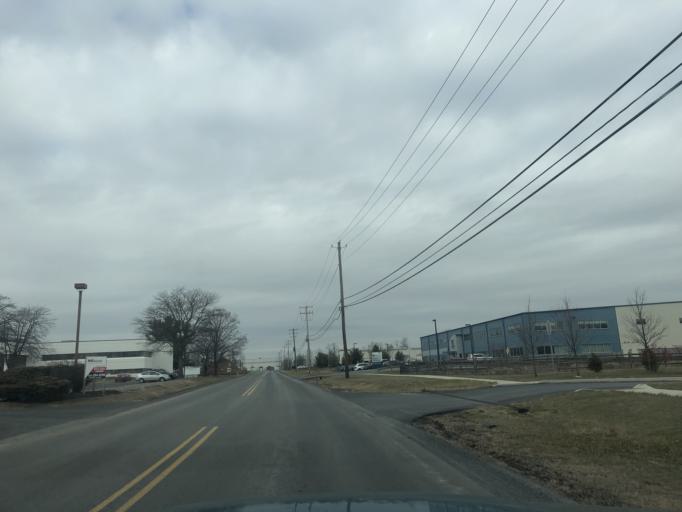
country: US
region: Pennsylvania
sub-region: Bucks County
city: Spinnerstown
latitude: 40.4381
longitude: -75.4196
